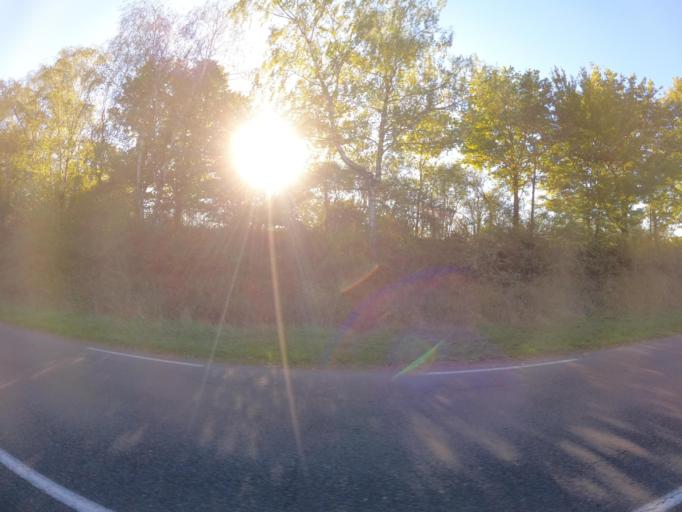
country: FR
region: Bourgogne
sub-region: Departement de Saone-et-Loire
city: Torcy
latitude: 46.7539
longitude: 4.4405
